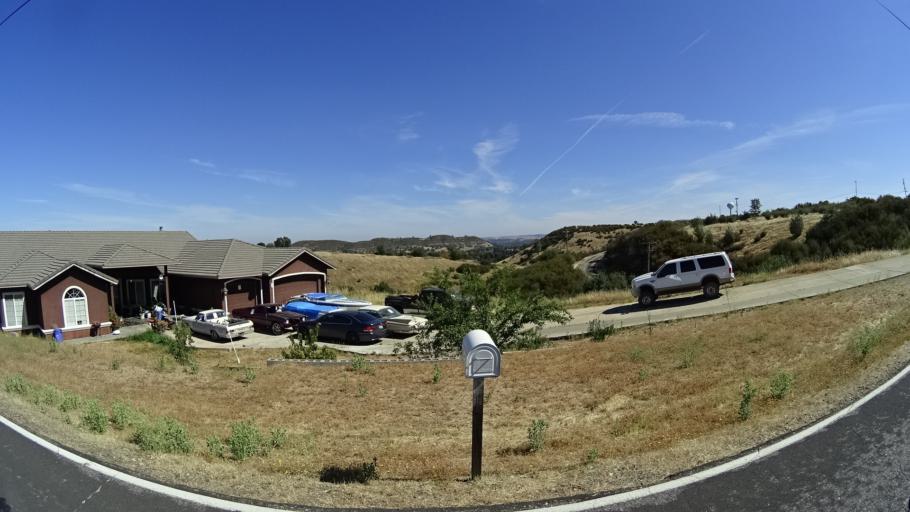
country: US
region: California
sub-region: Calaveras County
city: Valley Springs
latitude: 38.1725
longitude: -120.8634
